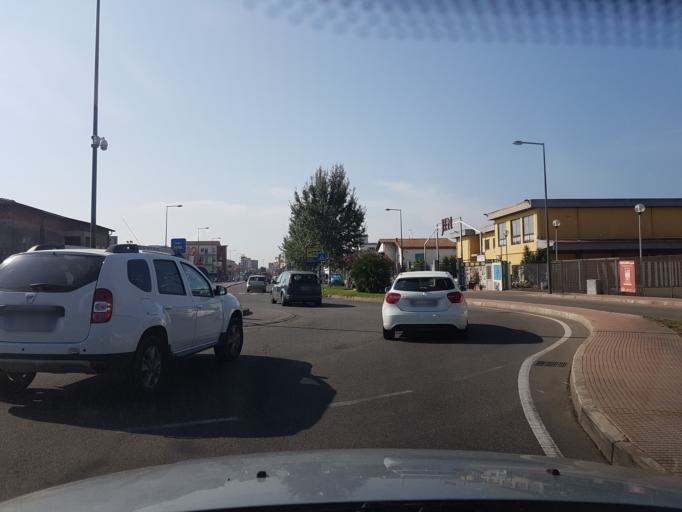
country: IT
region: Sardinia
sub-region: Provincia di Oristano
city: Oristano
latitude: 39.9149
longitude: 8.5855
